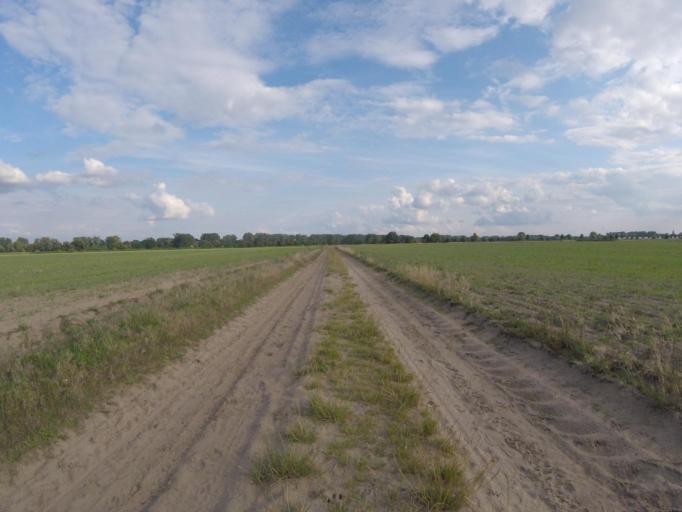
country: DE
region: Brandenburg
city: Mittenwalde
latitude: 52.2824
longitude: 13.5544
